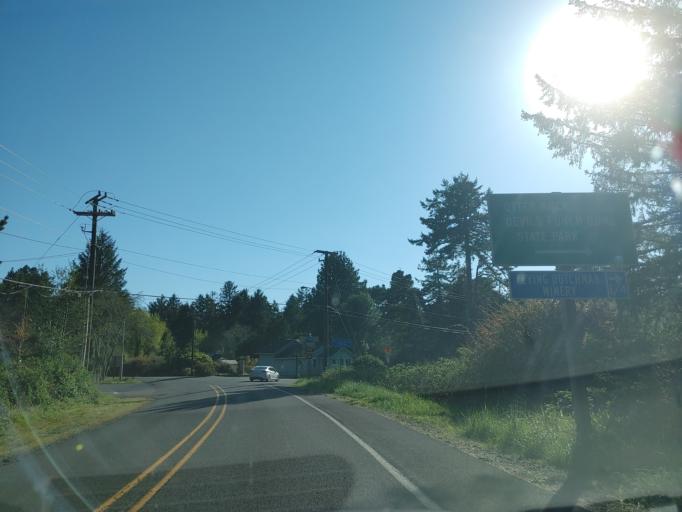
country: US
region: Oregon
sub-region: Lincoln County
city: Depoe Bay
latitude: 44.7474
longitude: -124.0554
